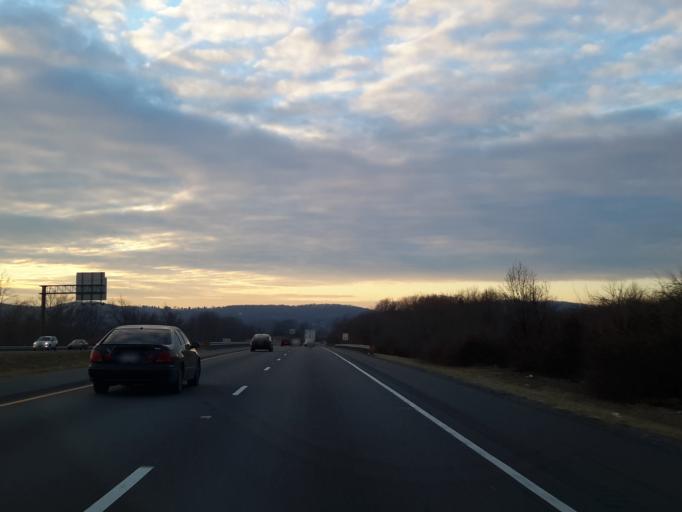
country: US
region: Maryland
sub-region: Frederick County
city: Ballenger Creek
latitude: 39.4033
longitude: -77.4547
